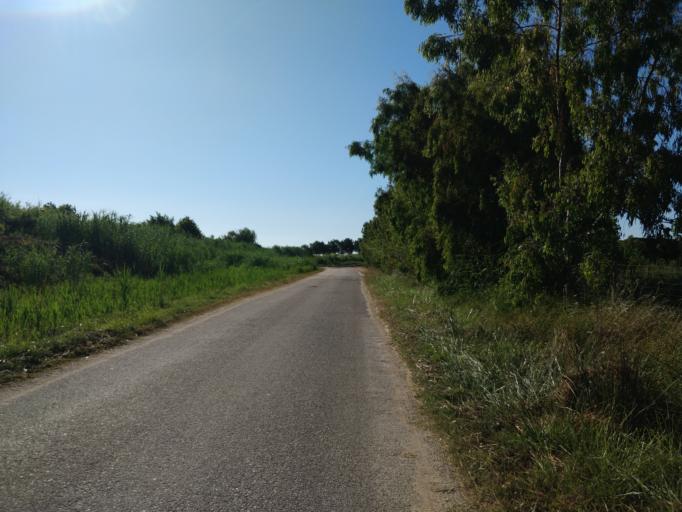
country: IT
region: Sardinia
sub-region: Provincia di Ogliastra
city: Lotzorai
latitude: 39.9600
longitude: 9.6811
